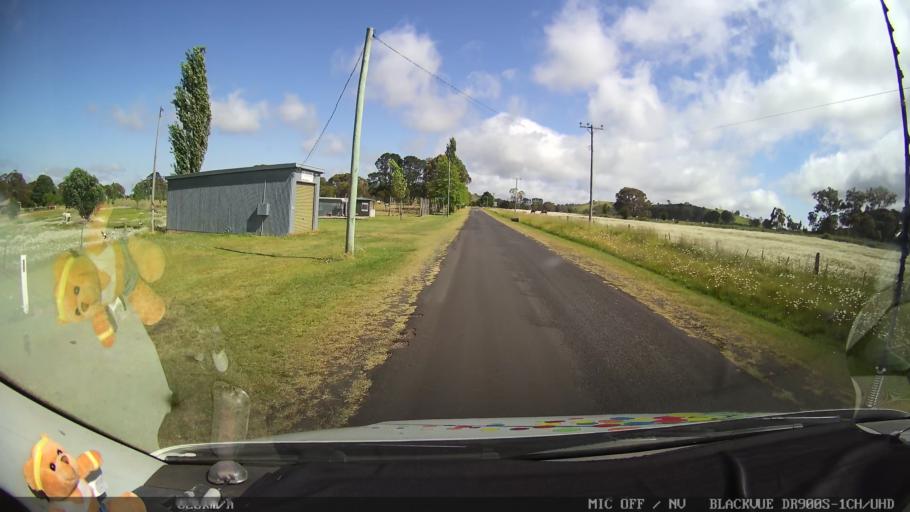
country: AU
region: New South Wales
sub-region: Guyra
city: Guyra
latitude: -30.0192
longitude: 151.6586
